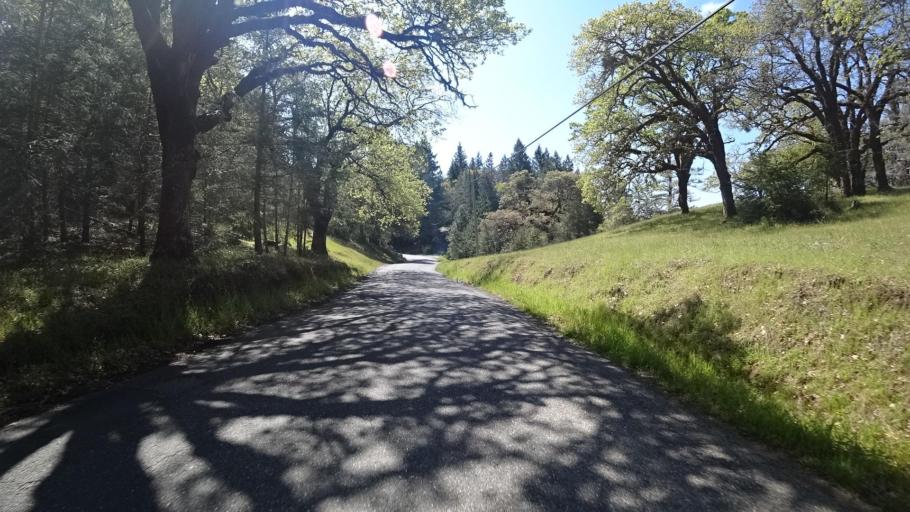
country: US
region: California
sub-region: Humboldt County
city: Redway
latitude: 40.0347
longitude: -123.6403
